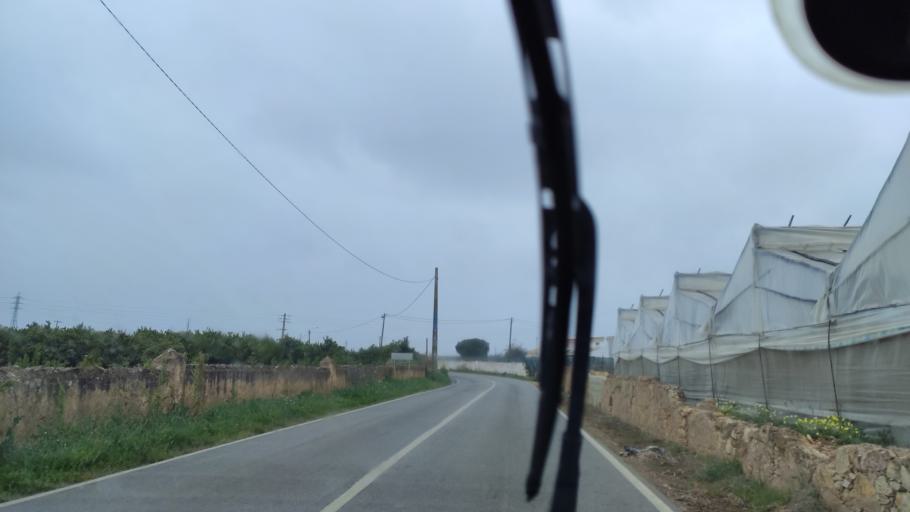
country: PT
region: Faro
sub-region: Faro
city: Santa Barbara de Nexe
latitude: 37.0737
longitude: -7.9439
